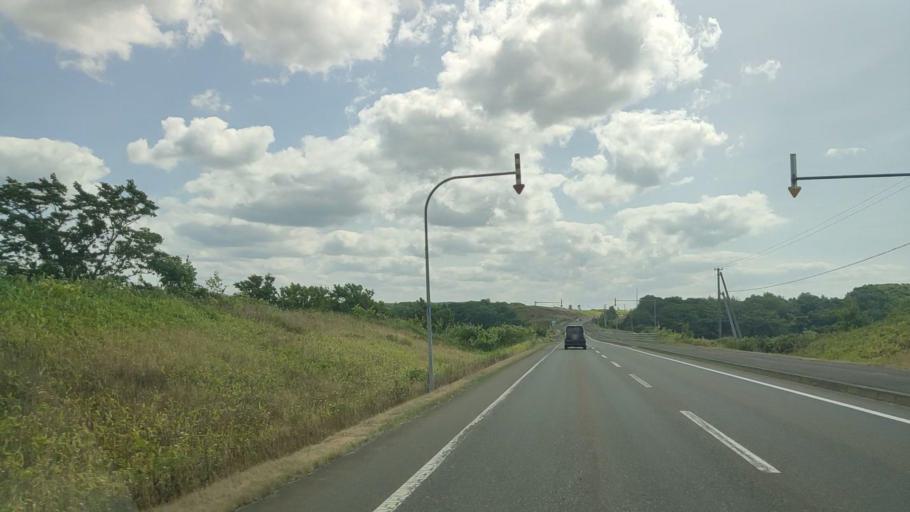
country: JP
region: Hokkaido
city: Makubetsu
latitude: 44.7953
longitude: 141.7891
